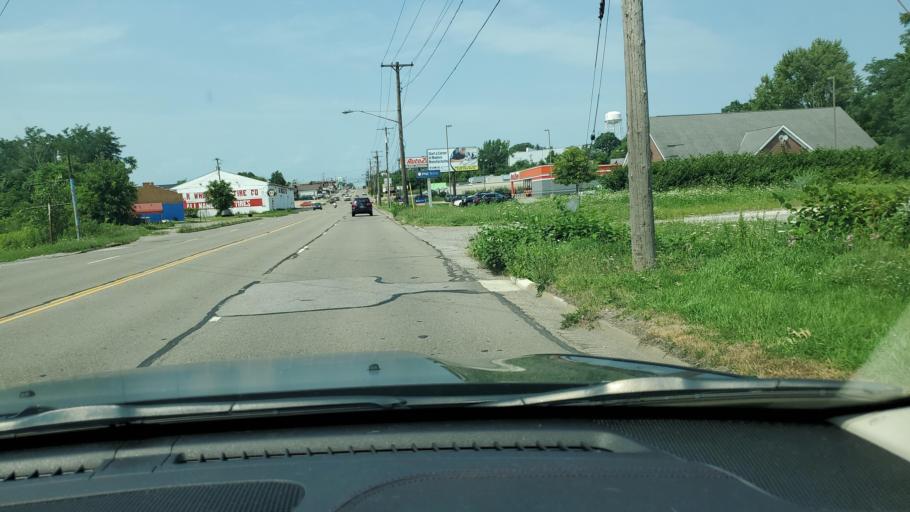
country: US
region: Ohio
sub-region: Mahoning County
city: Austintown
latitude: 41.0984
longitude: -80.7109
